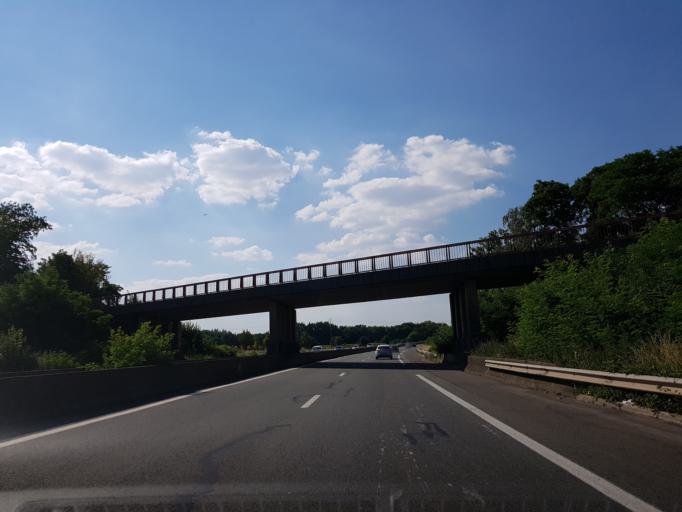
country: FR
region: Nord-Pas-de-Calais
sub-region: Departement du Nord
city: Escaudain
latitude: 50.3334
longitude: 3.3242
